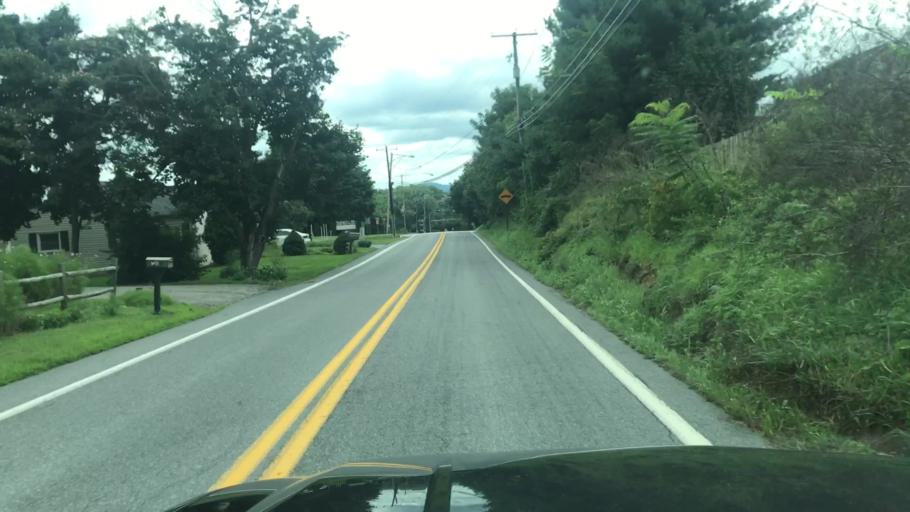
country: US
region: Pennsylvania
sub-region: Cumberland County
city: Enola
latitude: 40.2685
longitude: -76.9825
